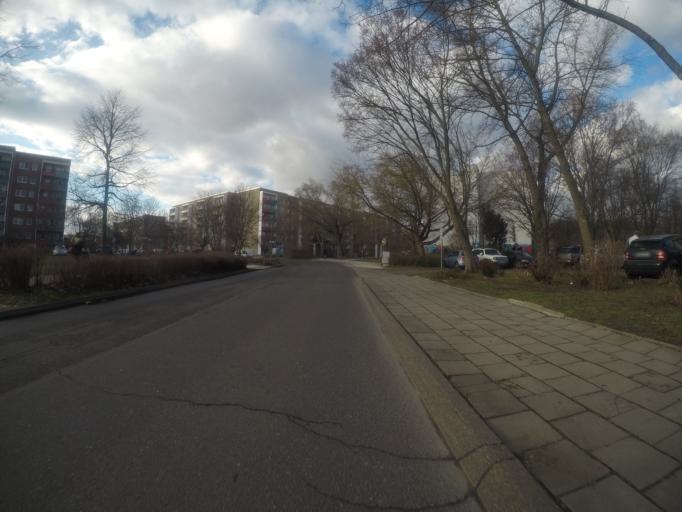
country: DE
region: Berlin
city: Marzahn
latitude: 52.5502
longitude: 13.5827
